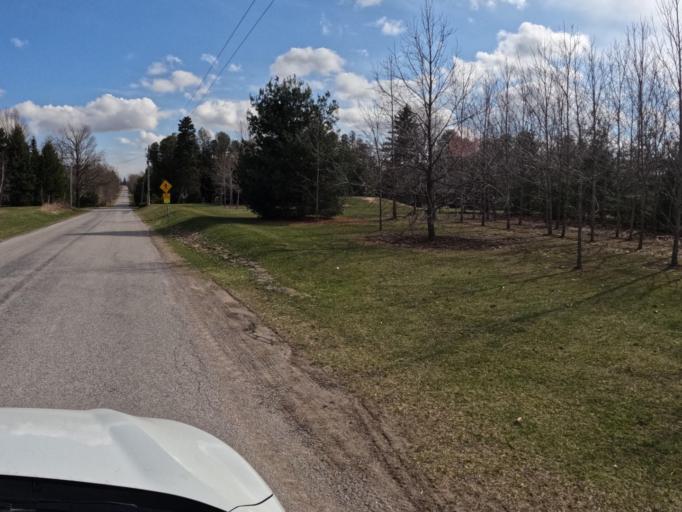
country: CA
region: Ontario
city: Norfolk County
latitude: 42.8957
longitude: -80.2874
